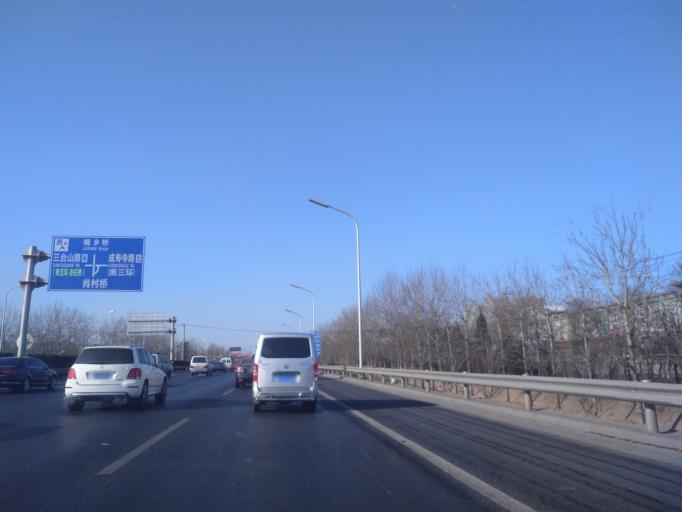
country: CN
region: Beijing
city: Jiugong
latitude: 39.8321
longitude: 116.4522
